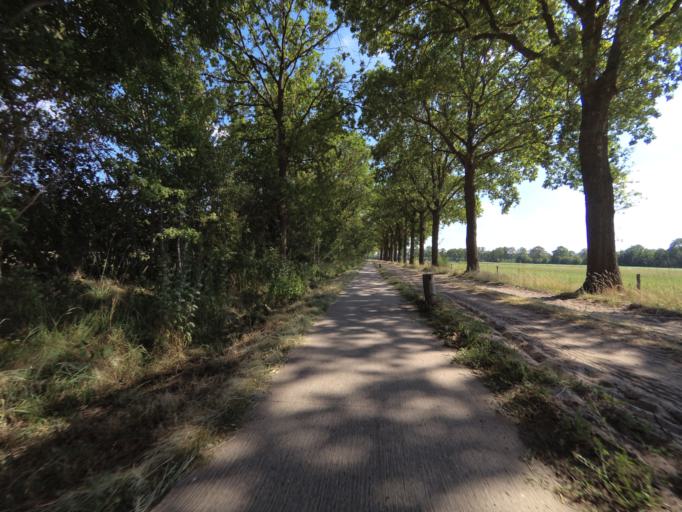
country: NL
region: Overijssel
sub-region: Gemeente Oldenzaal
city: Oldenzaal
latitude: 52.3697
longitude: 6.9002
